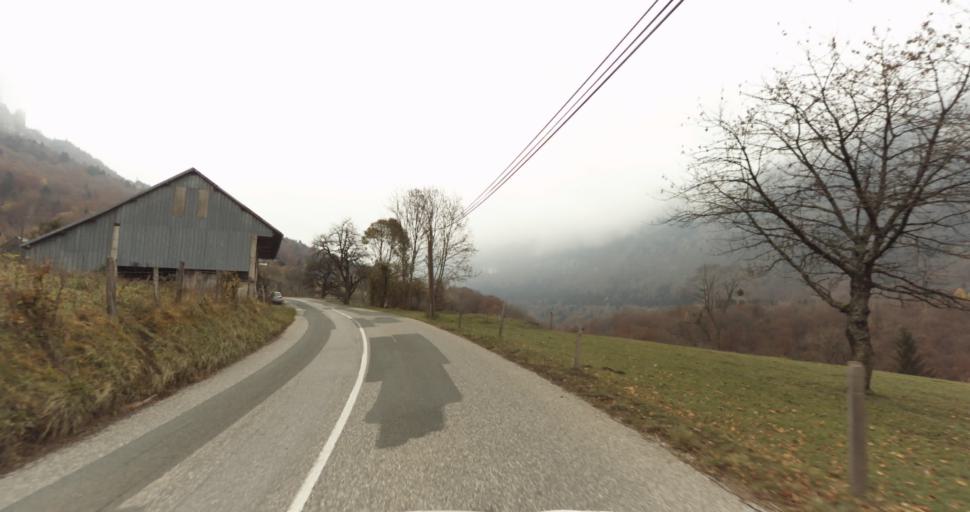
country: FR
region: Rhone-Alpes
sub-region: Departement de la Haute-Savoie
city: Gruffy
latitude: 45.7622
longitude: 6.0625
